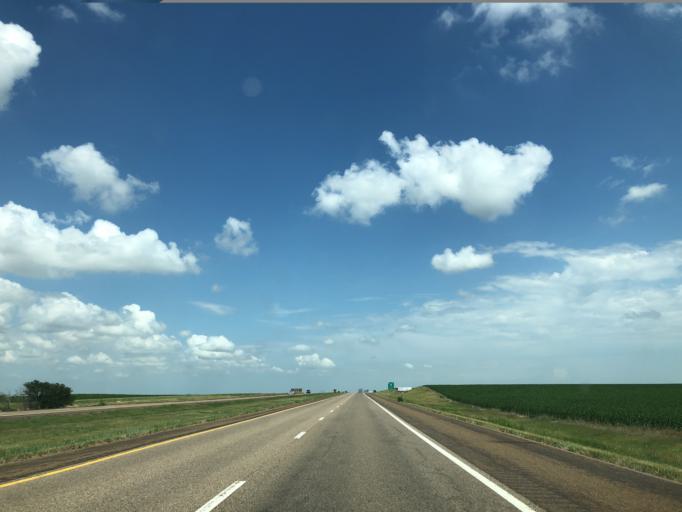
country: US
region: Kansas
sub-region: Thomas County
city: Colby
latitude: 39.3660
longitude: -101.2293
